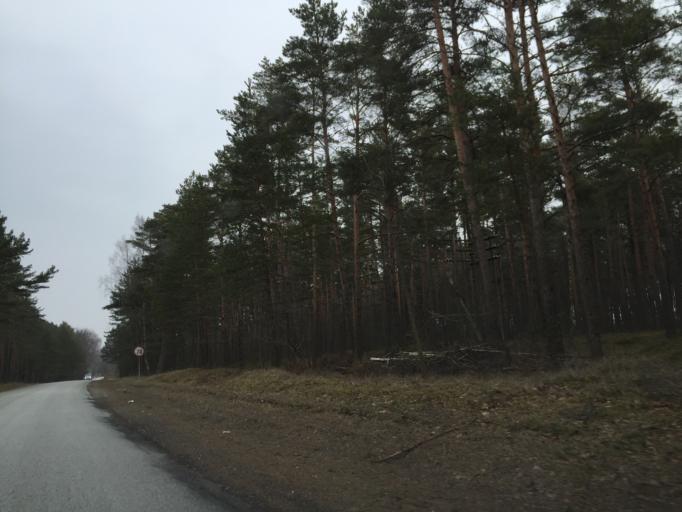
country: LV
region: Salacgrivas
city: Ainazi
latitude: 58.0316
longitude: 24.4599
